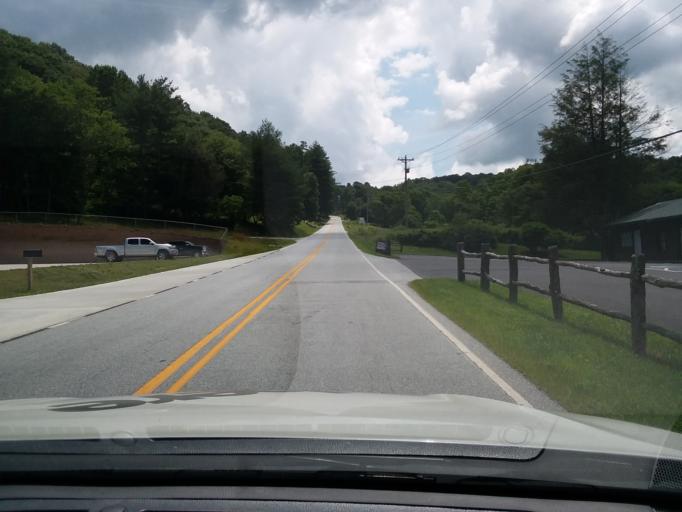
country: US
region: Georgia
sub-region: Rabun County
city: Mountain City
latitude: 35.0220
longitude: -83.3045
